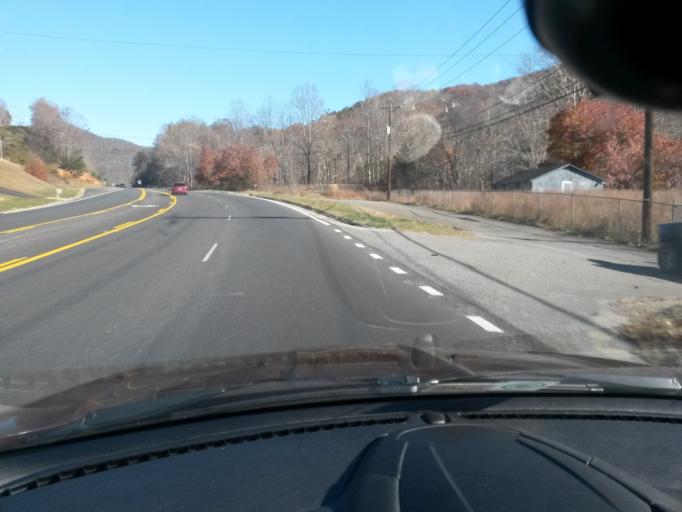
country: US
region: Virginia
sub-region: Patrick County
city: Stuart
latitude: 36.6596
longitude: -80.2766
